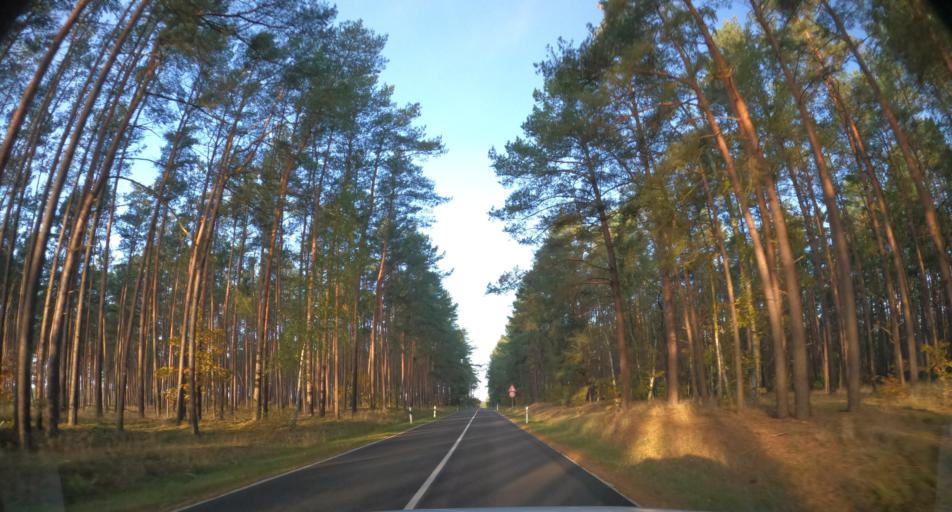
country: DE
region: Mecklenburg-Vorpommern
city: Ahlbeck
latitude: 53.6798
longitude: 14.1797
